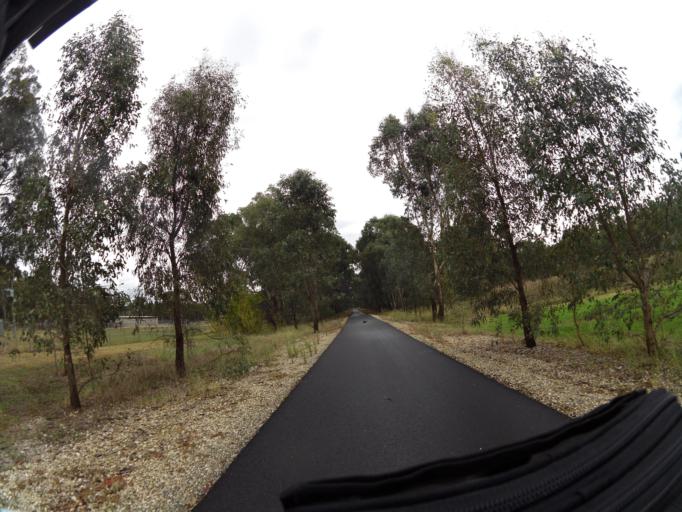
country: AU
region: Victoria
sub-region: Wodonga
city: Wodonga
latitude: -36.1445
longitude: 146.9180
